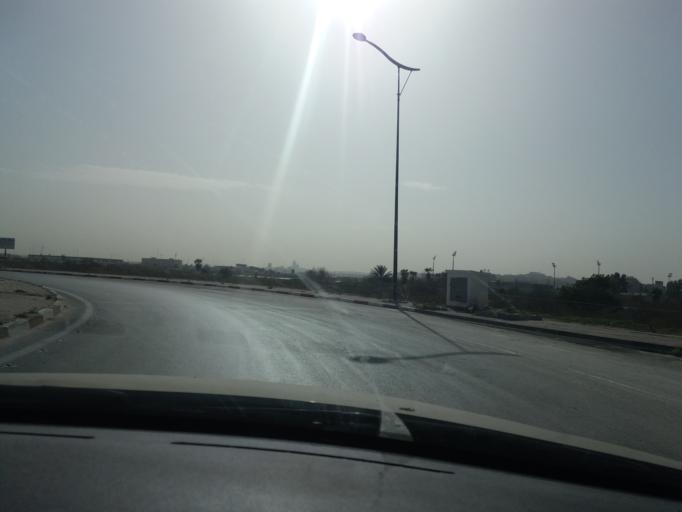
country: TN
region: Tunis
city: Tunis
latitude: 36.8072
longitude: 10.1932
